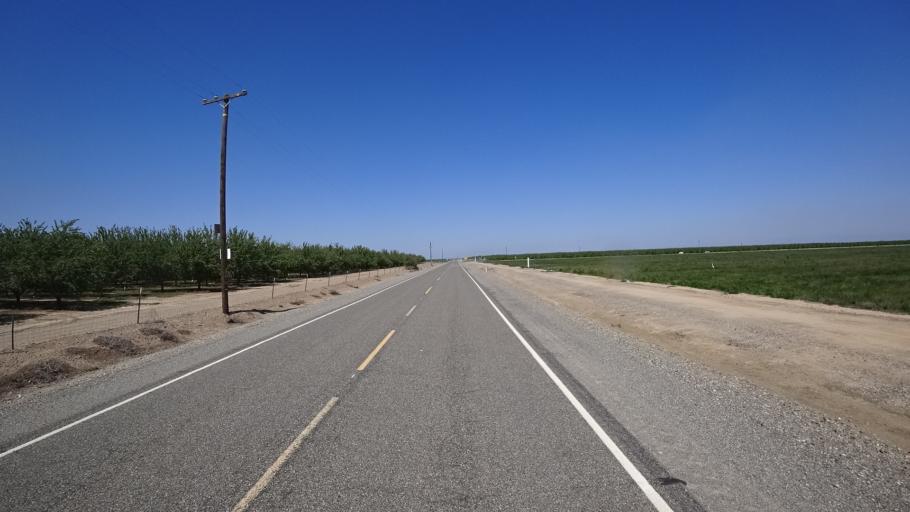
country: US
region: California
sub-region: Glenn County
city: Willows
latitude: 39.5796
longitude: -122.1371
